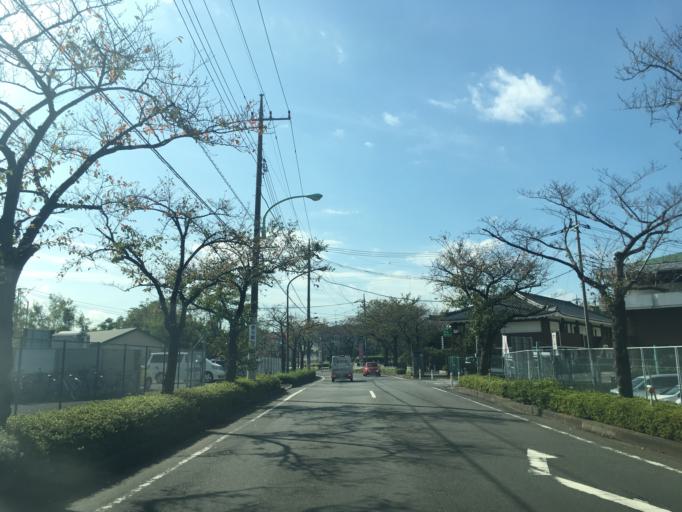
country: JP
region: Tokyo
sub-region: Machida-shi
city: Machida
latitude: 35.5856
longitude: 139.4101
